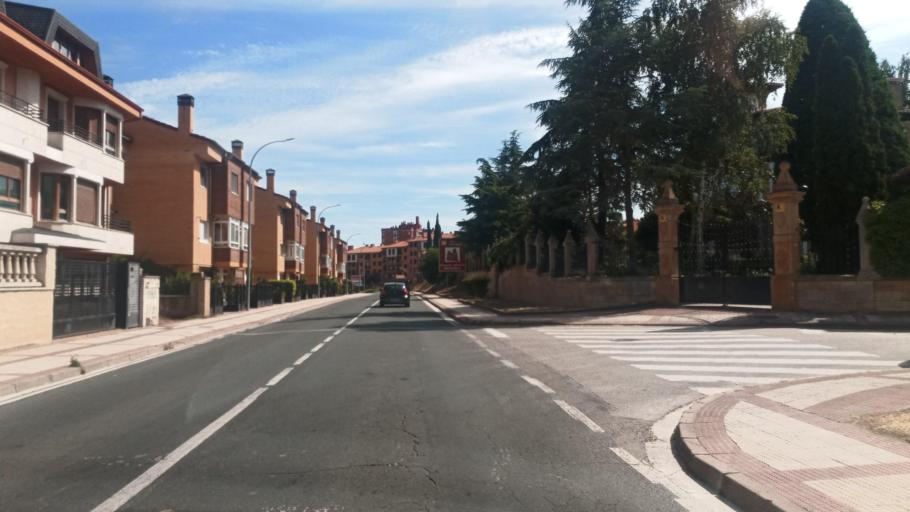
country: ES
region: Castille and Leon
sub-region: Provincia de Burgos
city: Briviesca
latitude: 42.5551
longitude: -3.3269
